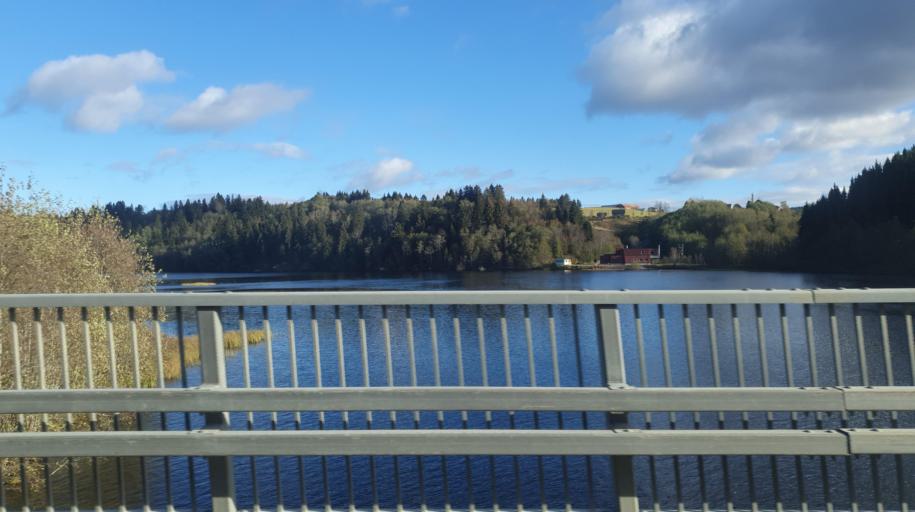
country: NO
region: Sor-Trondelag
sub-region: Klaebu
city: Klaebu
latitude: 63.3110
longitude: 10.4520
